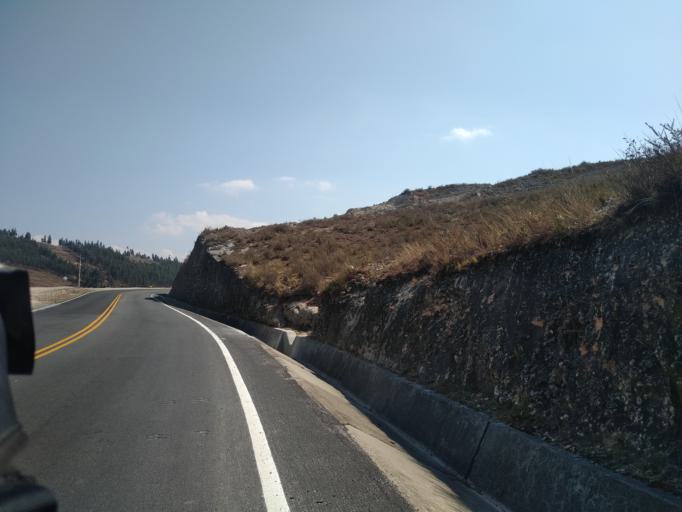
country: PE
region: Cajamarca
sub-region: Provincia de Cajamarca
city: Llacanora
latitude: -7.2088
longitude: -78.3933
